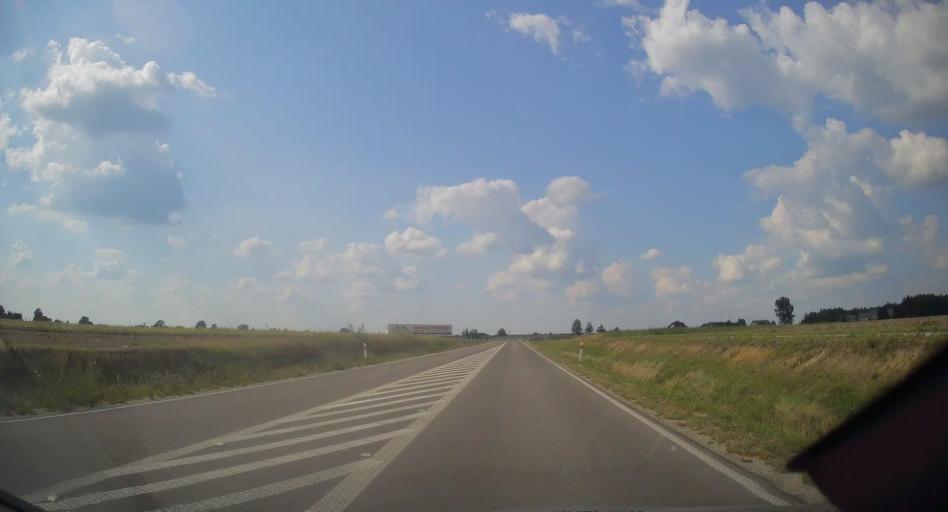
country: PL
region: Swietokrzyskie
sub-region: Powiat kielecki
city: Lopuszno
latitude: 50.9729
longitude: 20.2490
